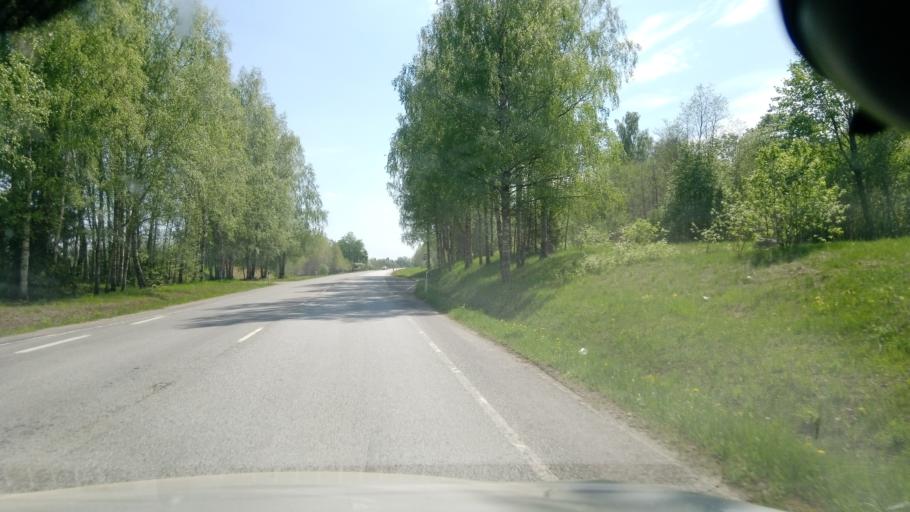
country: EE
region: Laeaene-Virumaa
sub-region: Haljala vald
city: Haljala
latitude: 59.4036
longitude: 26.3018
